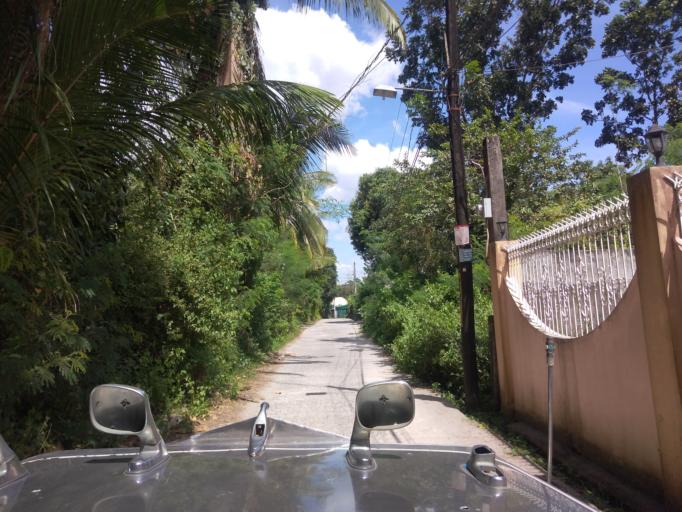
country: PH
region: Central Luzon
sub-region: Province of Pampanga
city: San Basilio
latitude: 15.0142
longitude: 120.5877
